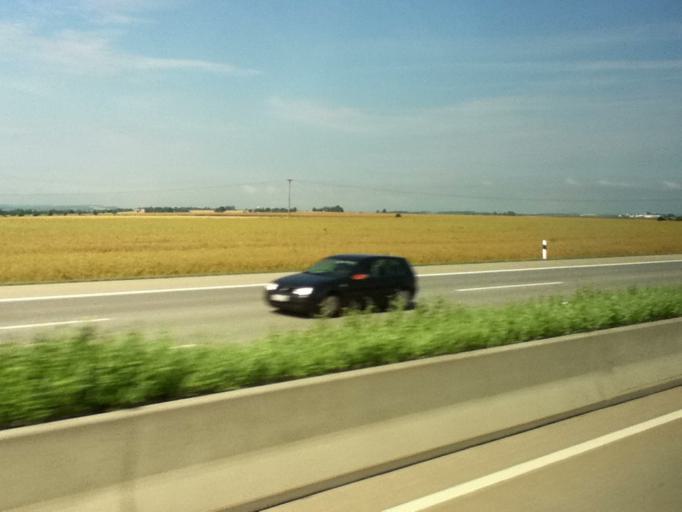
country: DE
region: Thuringia
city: Ronneburg
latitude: 50.8789
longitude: 12.1616
